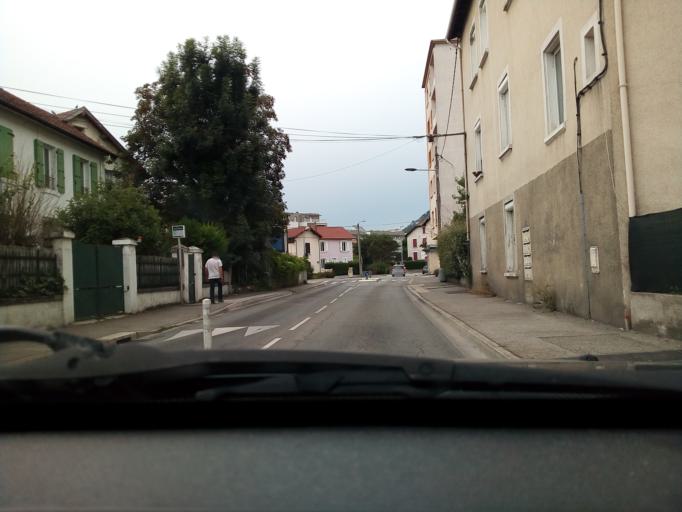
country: FR
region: Rhone-Alpes
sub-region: Departement de l'Isere
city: Saint-Martin-d'Heres
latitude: 45.1817
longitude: 5.7488
